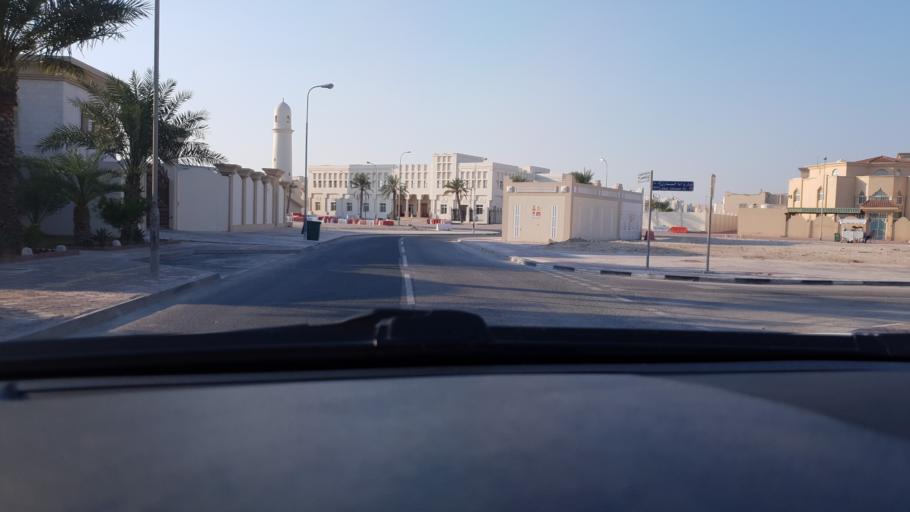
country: QA
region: Baladiyat ad Dawhah
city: Doha
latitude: 25.2353
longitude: 51.5573
